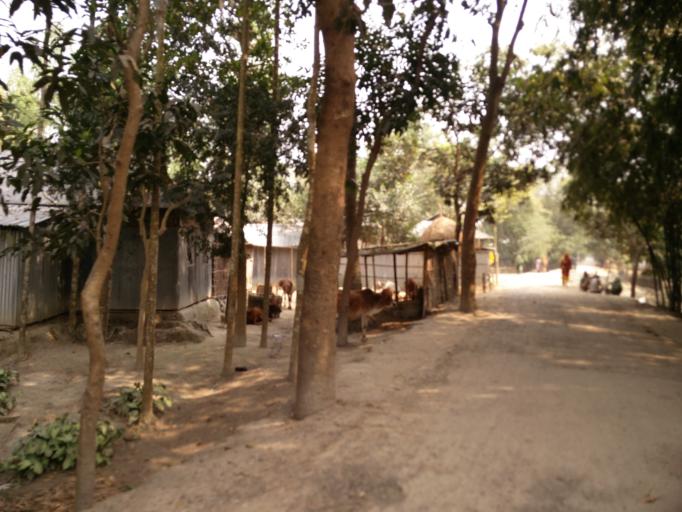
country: BD
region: Rangpur Division
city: Nageswari
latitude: 25.8899
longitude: 89.7206
